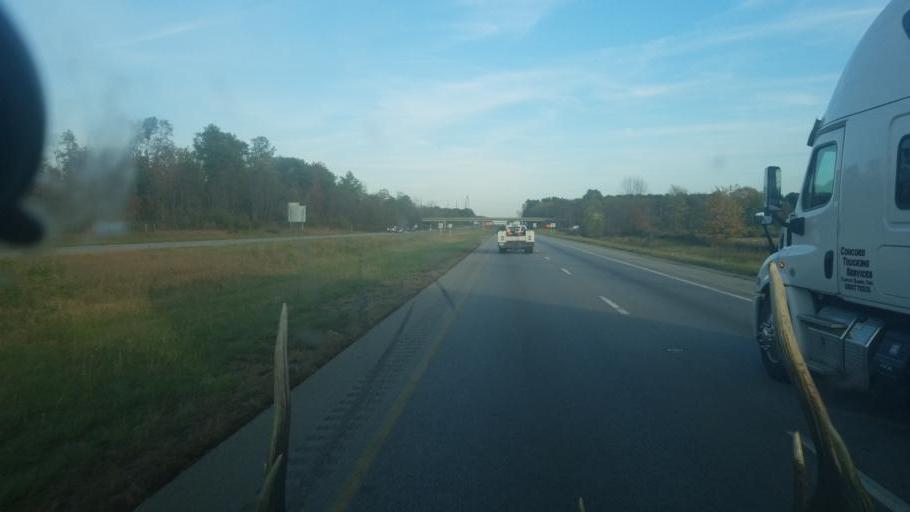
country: US
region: Ohio
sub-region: Licking County
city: Etna
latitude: 39.9481
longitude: -82.6726
